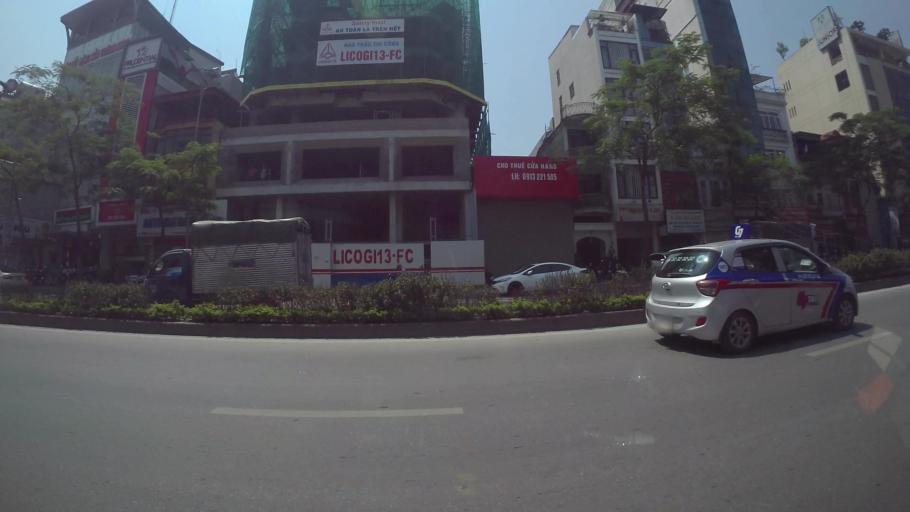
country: VN
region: Ha Noi
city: Hoan Kiem
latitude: 21.0411
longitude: 105.8687
